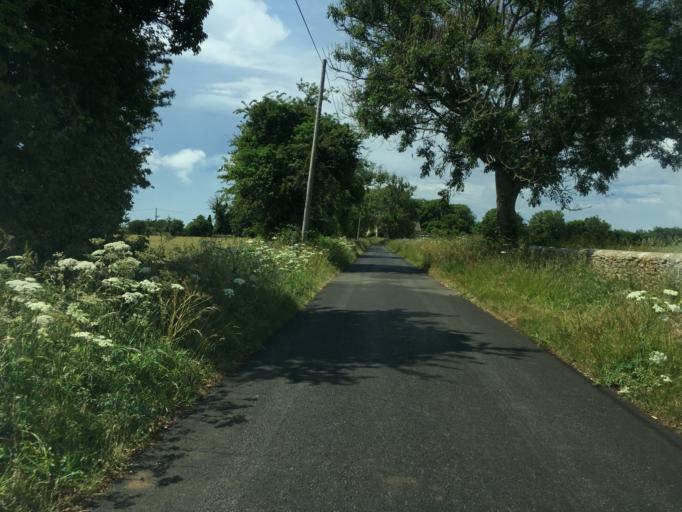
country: GB
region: England
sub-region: Gloucestershire
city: Tetbury
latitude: 51.6286
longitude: -2.2070
